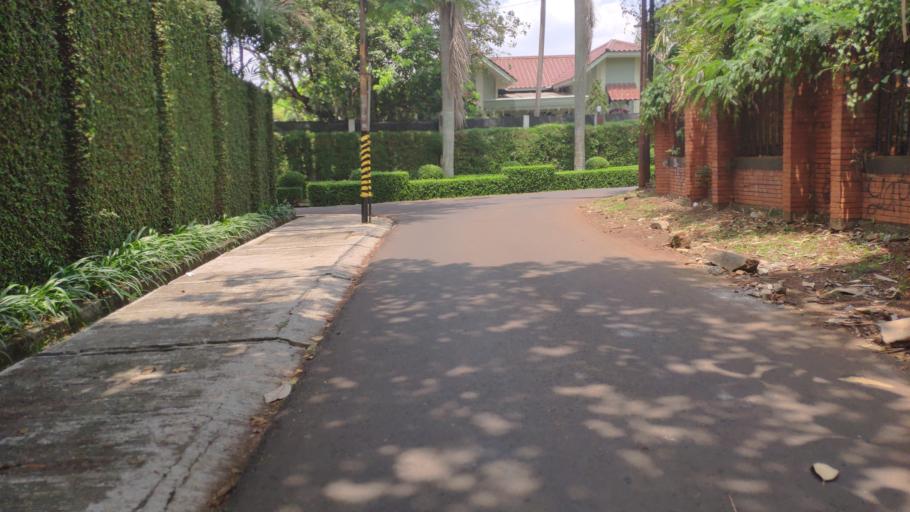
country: ID
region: Jakarta Raya
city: Jakarta
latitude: -6.2750
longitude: 106.8229
